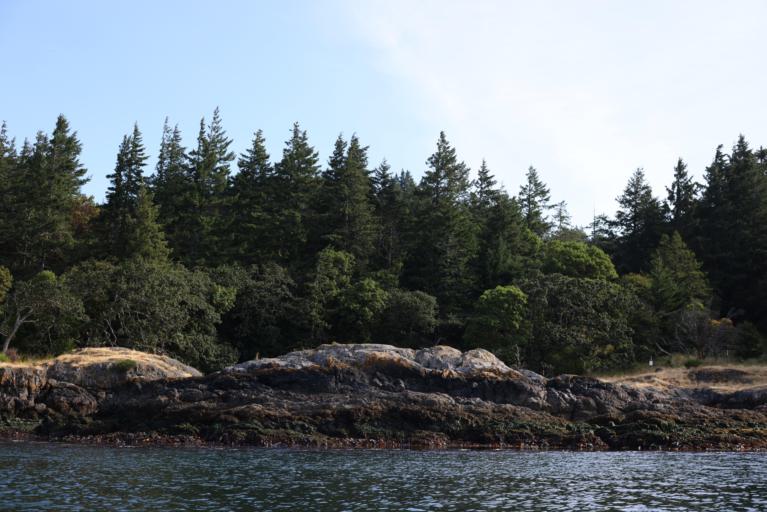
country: CA
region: British Columbia
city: Metchosin
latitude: 48.3394
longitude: -123.5525
